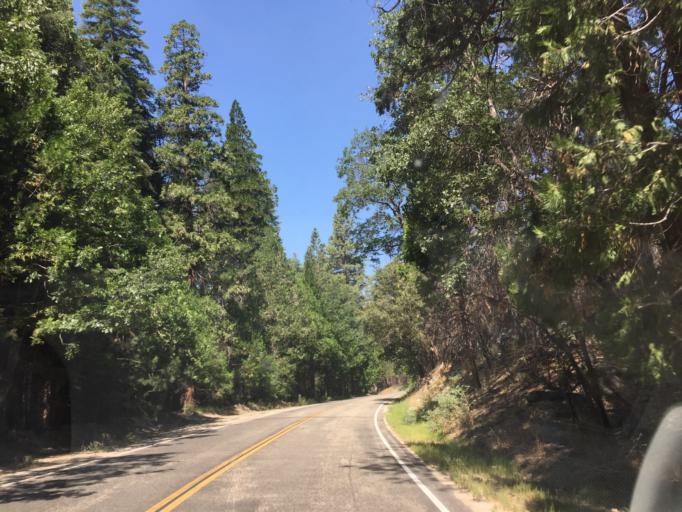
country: US
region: California
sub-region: Tulare County
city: Three Rivers
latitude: 36.8027
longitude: -118.6999
